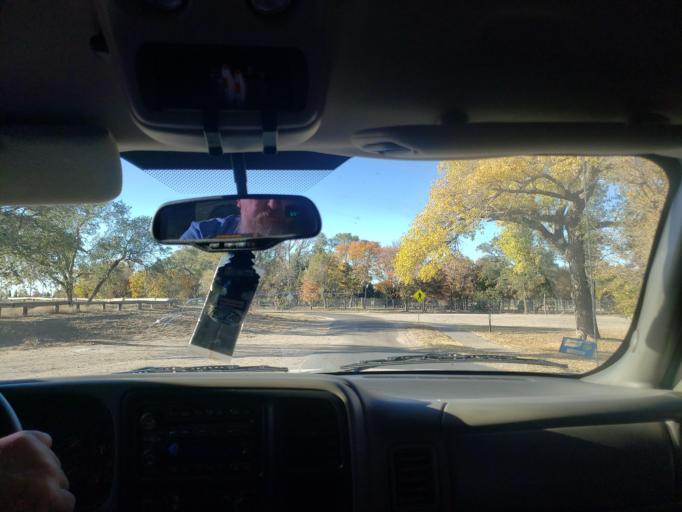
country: US
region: Kansas
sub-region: Finney County
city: Garden City
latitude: 37.9565
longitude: -100.8749
